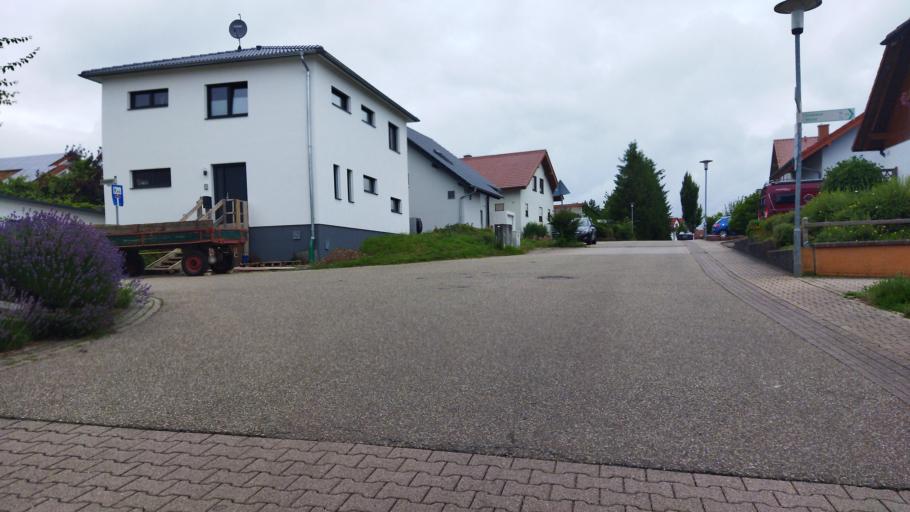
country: DE
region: Baden-Wuerttemberg
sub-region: Karlsruhe Region
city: Sinsheim
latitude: 49.1960
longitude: 8.8658
